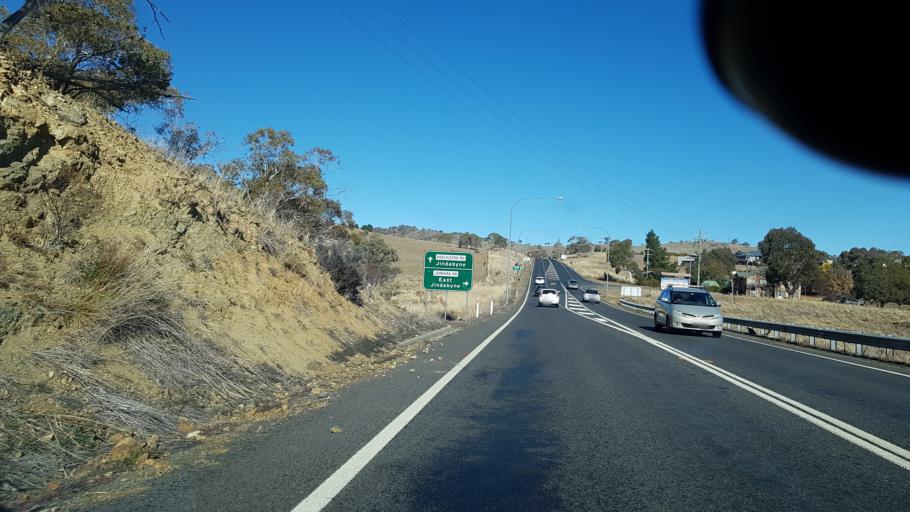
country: AU
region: New South Wales
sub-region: Snowy River
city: Jindabyne
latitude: -36.4004
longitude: 148.6533
